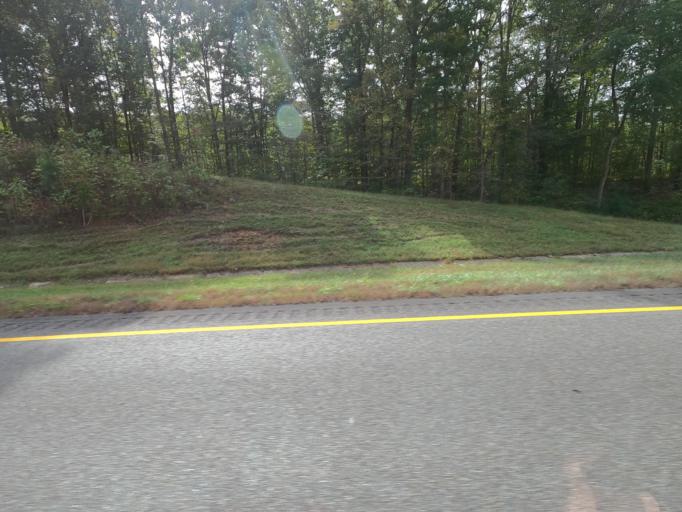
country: US
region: Tennessee
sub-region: Decatur County
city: Parsons
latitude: 35.8151
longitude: -88.2129
